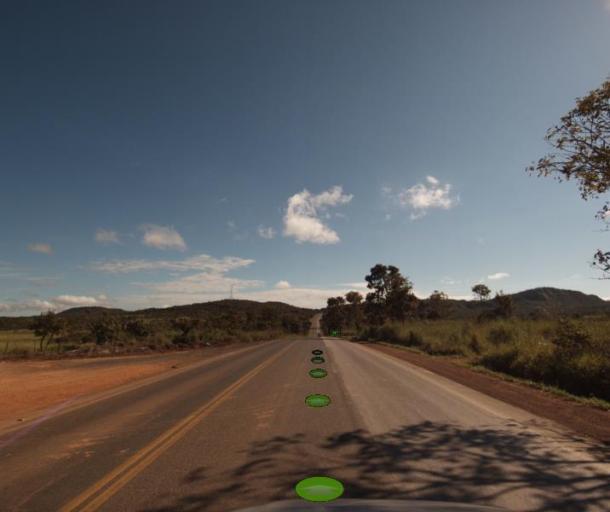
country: BR
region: Goias
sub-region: Uruacu
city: Uruacu
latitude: -14.5837
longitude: -49.1604
